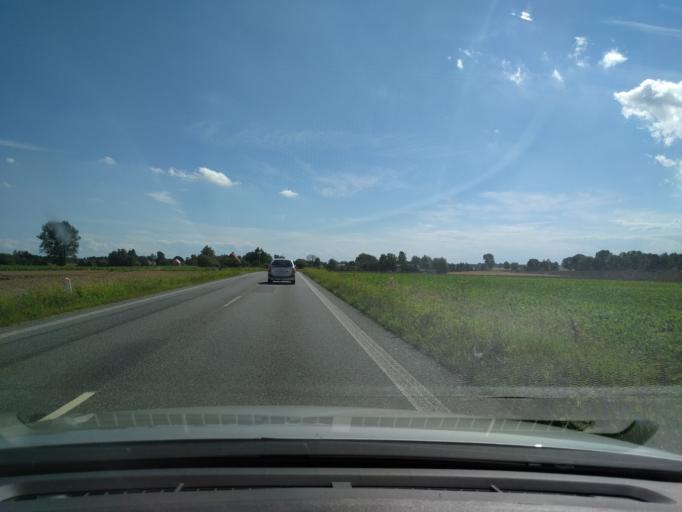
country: DK
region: Zealand
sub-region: Guldborgsund Kommune
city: Stubbekobing
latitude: 54.8241
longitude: 11.9948
